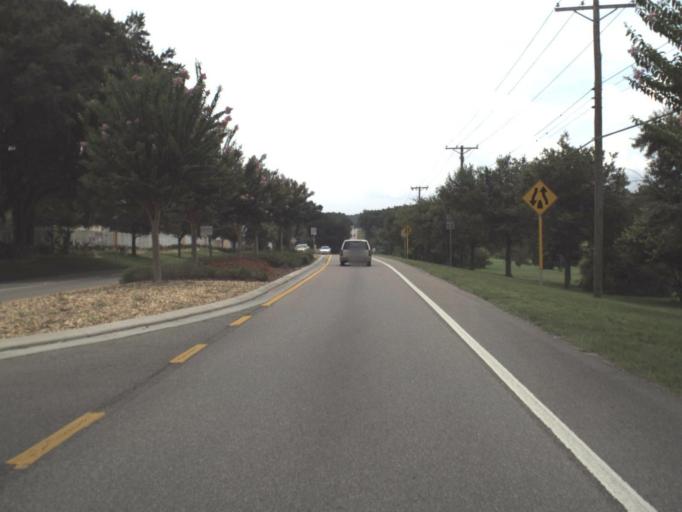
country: US
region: Florida
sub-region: Pasco County
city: Saint Leo
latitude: 28.3355
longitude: -82.2572
